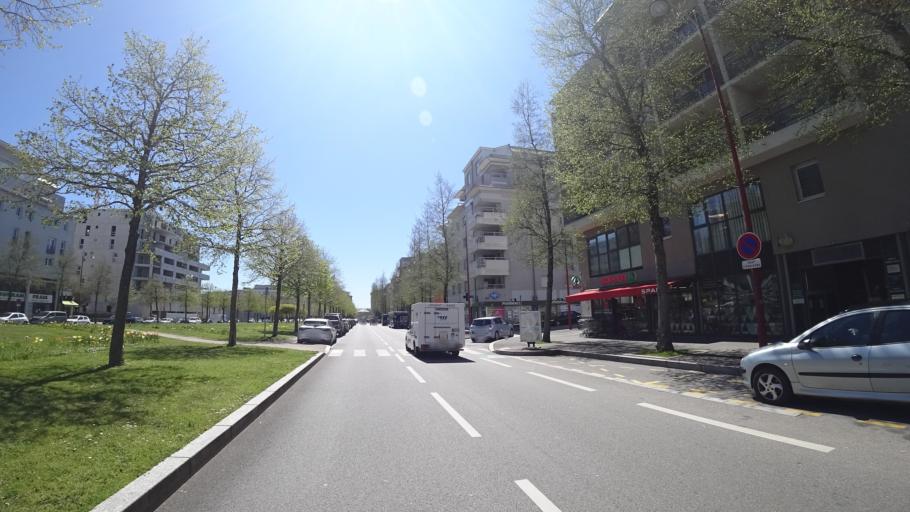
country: FR
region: Midi-Pyrenees
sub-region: Departement de l'Aveyron
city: Olemps
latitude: 44.3609
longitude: 2.5562
